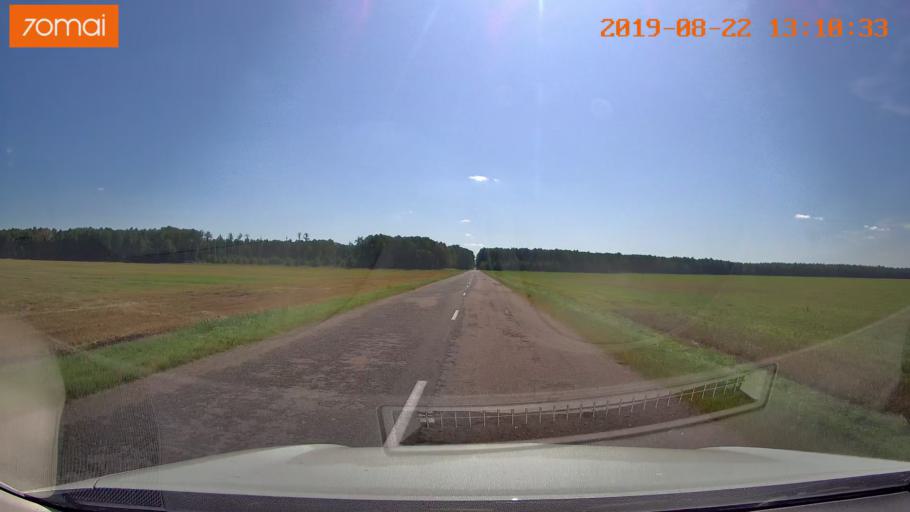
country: BY
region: Minsk
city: Prawdzinski
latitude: 53.2938
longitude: 27.8493
